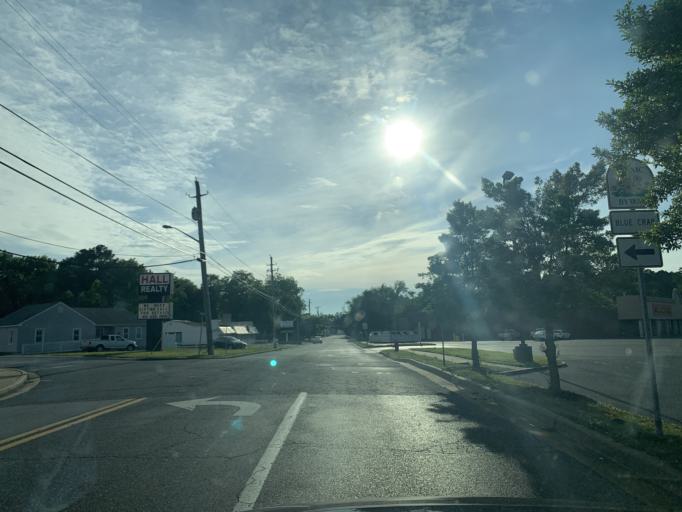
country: US
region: Maryland
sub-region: Worcester County
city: Pocomoke City
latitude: 38.0753
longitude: -75.5600
